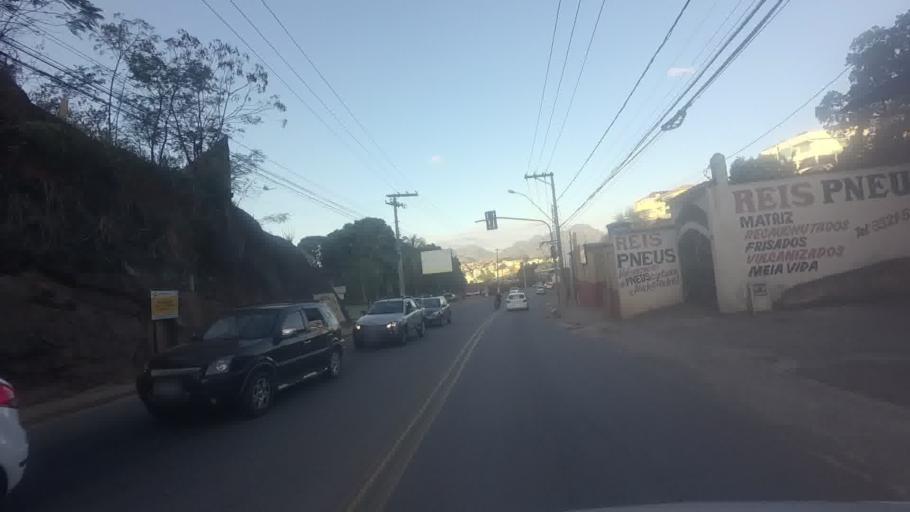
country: BR
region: Espirito Santo
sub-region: Cachoeiro De Itapemirim
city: Cachoeiro de Itapemirim
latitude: -20.8454
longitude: -41.1344
